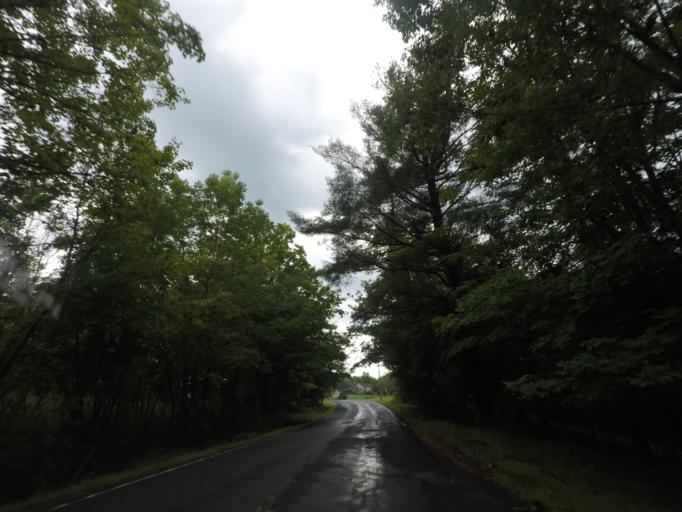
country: US
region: New York
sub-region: Rensselaer County
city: Poestenkill
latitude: 42.7451
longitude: -73.5941
